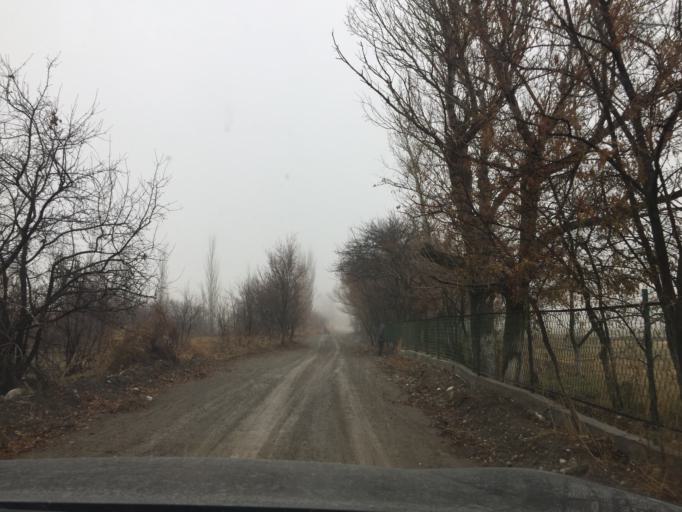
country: KZ
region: Ongtustik Qazaqstan
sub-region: Tulkibas Audany
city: Zhabagly
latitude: 42.5130
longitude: 70.5622
